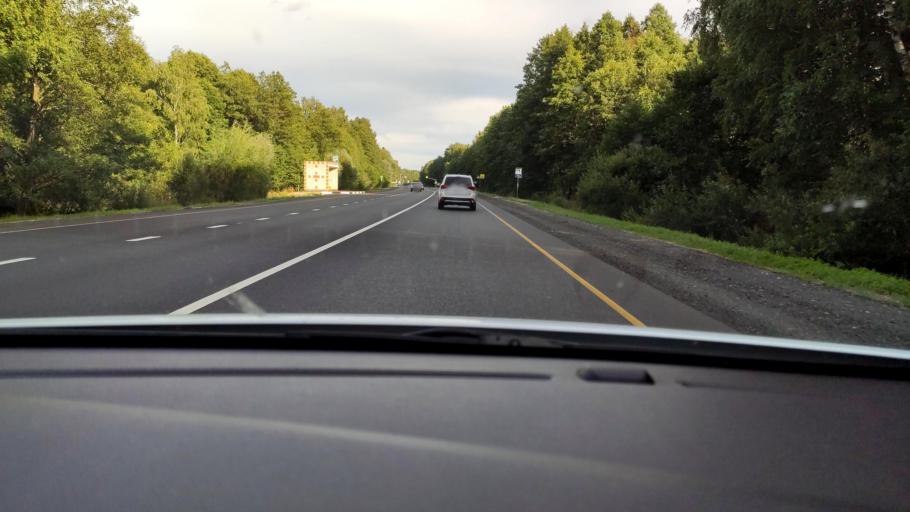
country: RU
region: Mariy-El
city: Krasnogorskiy
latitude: 56.1512
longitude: 48.3024
